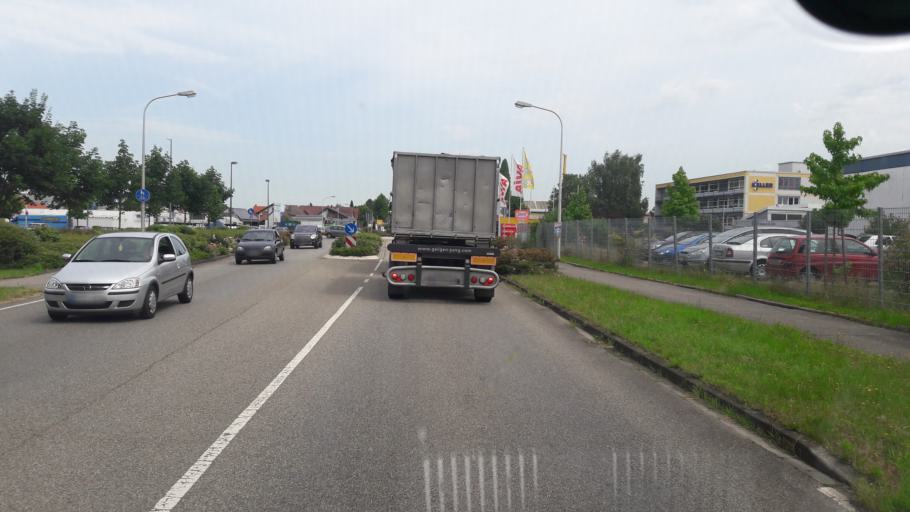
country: DE
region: Baden-Wuerttemberg
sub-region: Freiburg Region
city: Renchen
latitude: 48.5824
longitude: 8.0053
